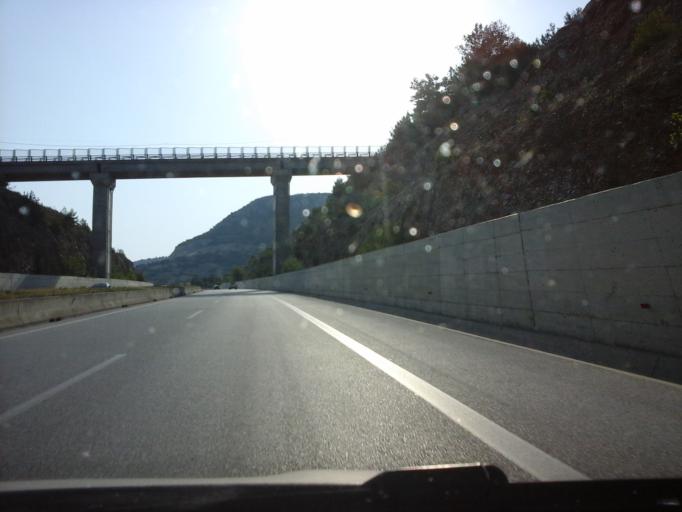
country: GR
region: East Macedonia and Thrace
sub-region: Nomos Kavalas
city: Chrysoupolis
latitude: 40.9914
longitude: 24.6144
